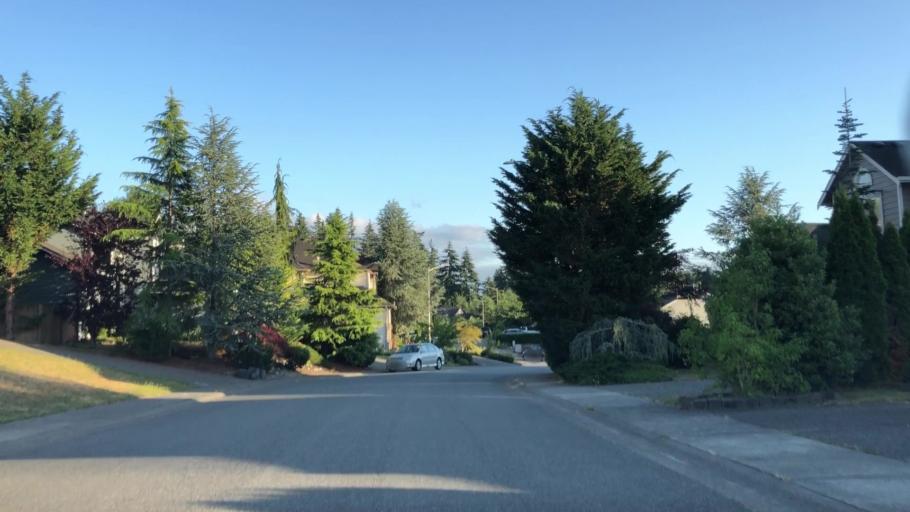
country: US
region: Washington
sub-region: Snohomish County
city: Martha Lake
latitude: 47.8635
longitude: -122.2631
